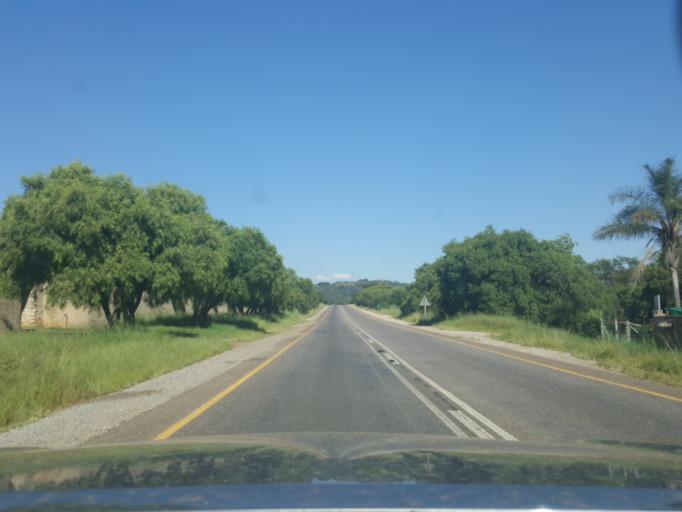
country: ZA
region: Gauteng
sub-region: City of Tshwane Metropolitan Municipality
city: Cullinan
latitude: -25.7755
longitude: 28.4660
